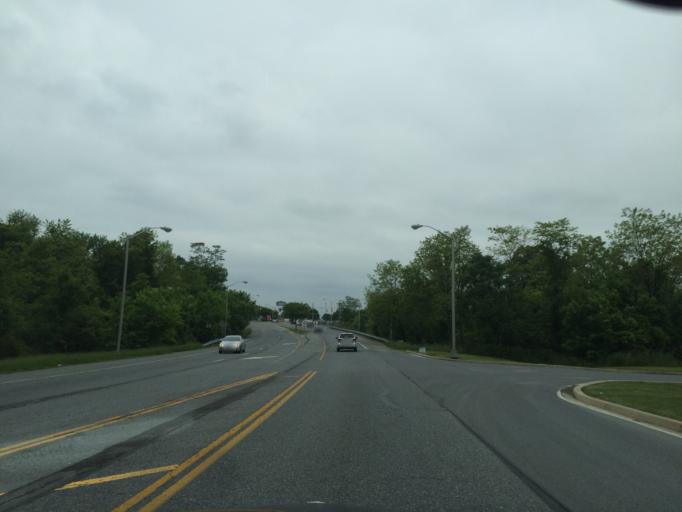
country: US
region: Maryland
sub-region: Washington County
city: Halfway
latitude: 39.6346
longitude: -77.7555
